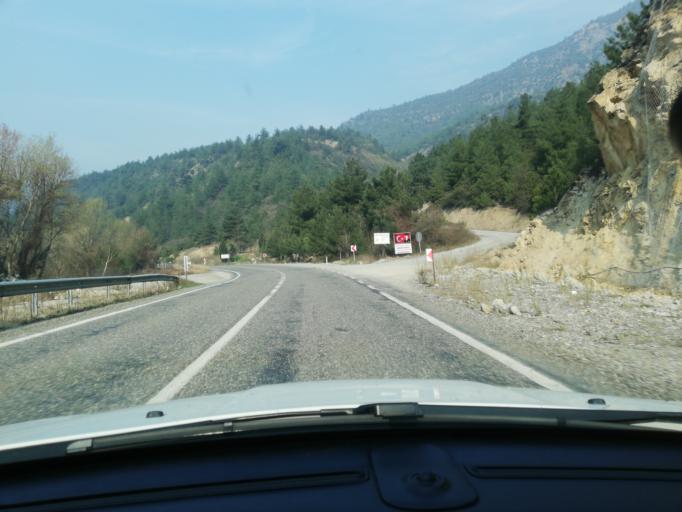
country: TR
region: Karabuk
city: Karabuk
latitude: 41.1588
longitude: 32.5485
